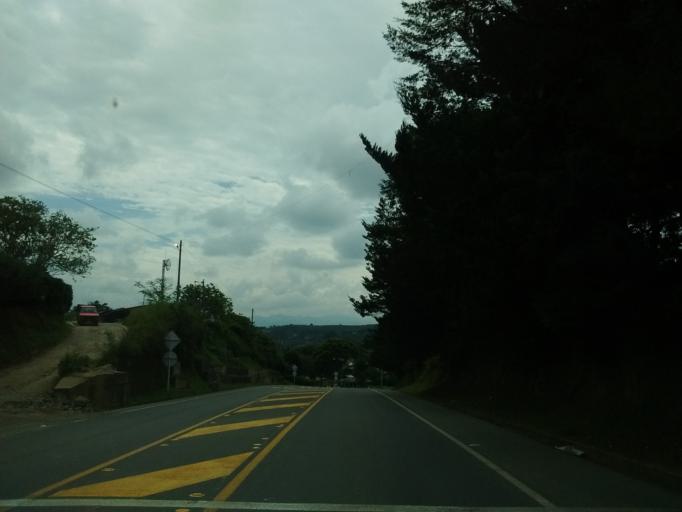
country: CO
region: Cauca
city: Cajibio
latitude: 2.5427
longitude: -76.5580
